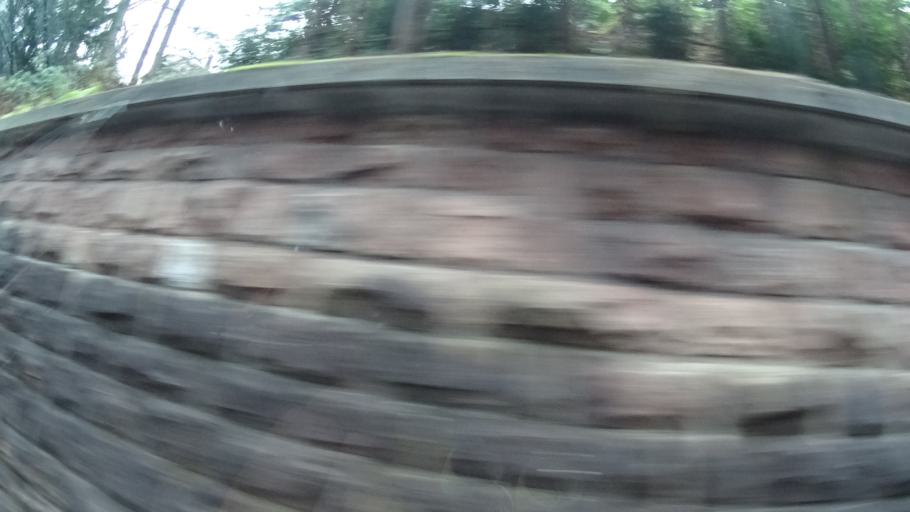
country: DE
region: Baden-Wuerttemberg
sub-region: Karlsruhe Region
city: Heidelberg
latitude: 49.4151
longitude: 8.7267
